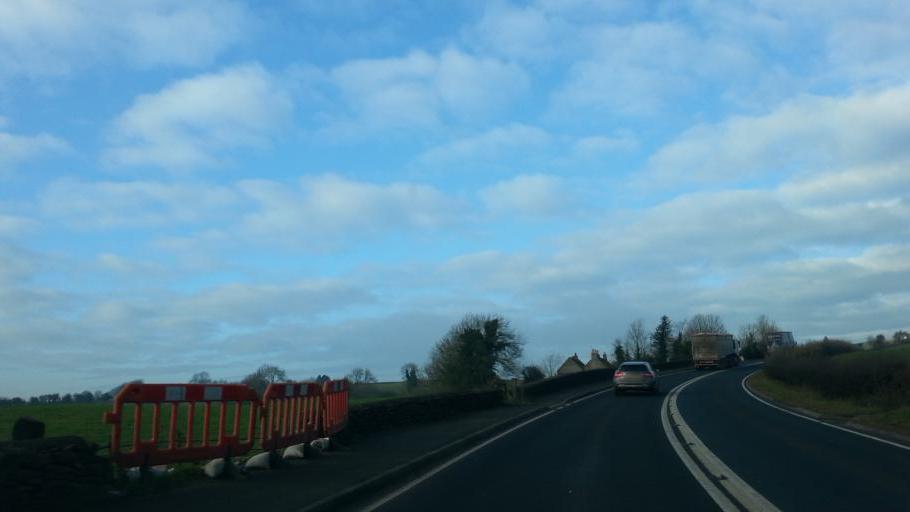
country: GB
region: England
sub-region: South Gloucestershire
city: Cold Ashton
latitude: 51.4460
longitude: -2.3652
